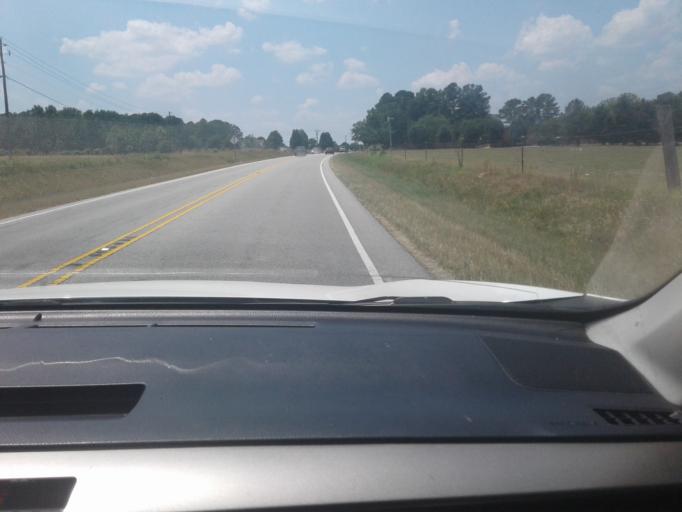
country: US
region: North Carolina
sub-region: Johnston County
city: Benson
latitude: 35.3903
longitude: -78.5828
